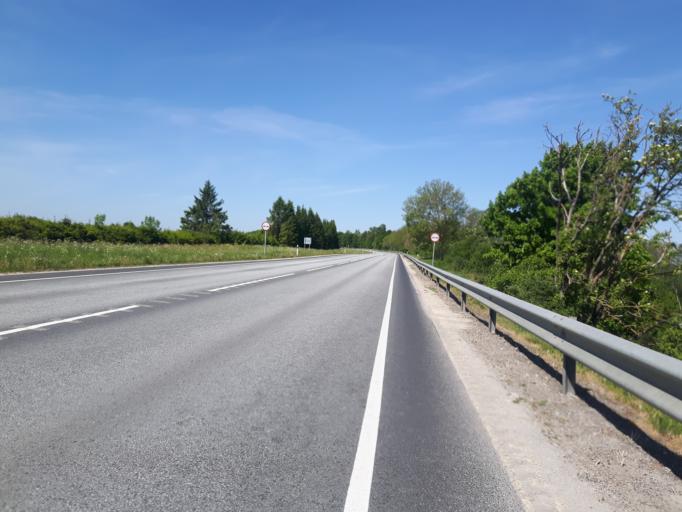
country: EE
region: Ida-Virumaa
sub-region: Aseri vald
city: Aseri
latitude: 59.4378
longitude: 26.9156
